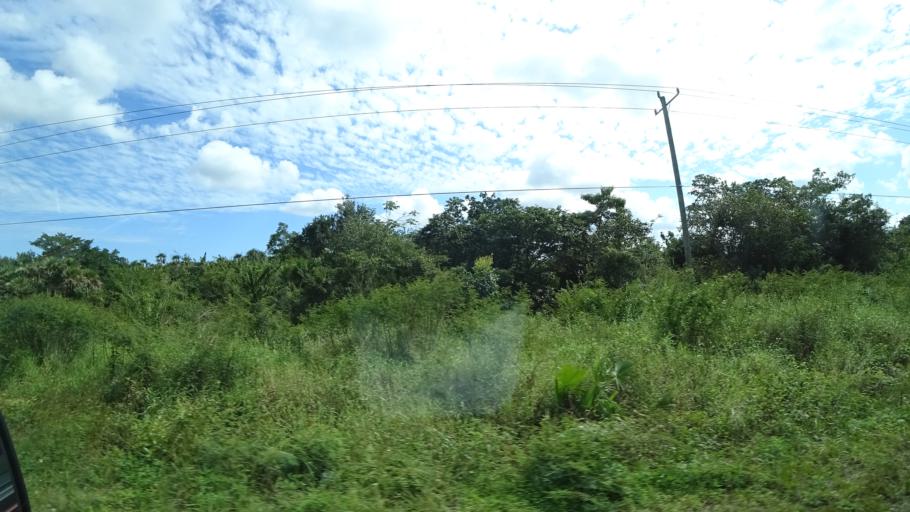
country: BZ
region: Belize
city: Belize City
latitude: 17.5643
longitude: -88.4022
